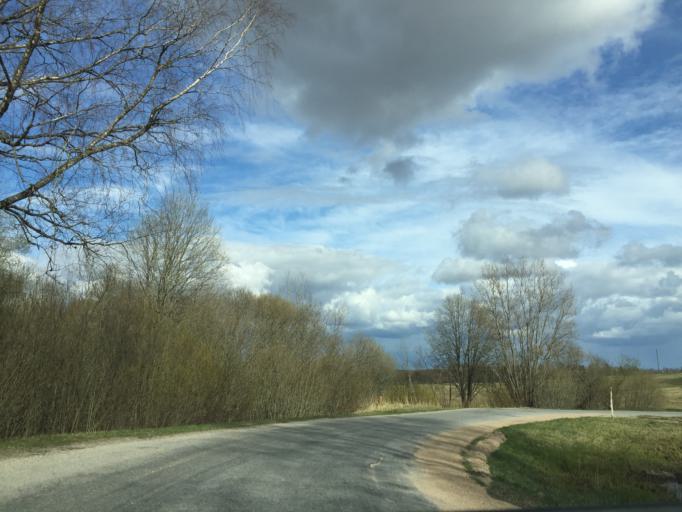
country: LV
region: Limbazu Rajons
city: Limbazi
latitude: 57.5979
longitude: 24.8258
